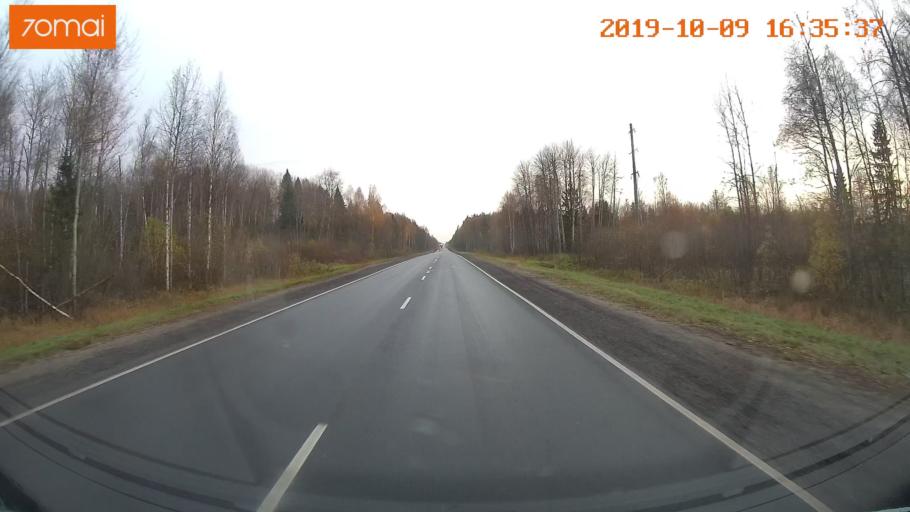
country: RU
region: Kostroma
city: Volgorechensk
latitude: 57.5530
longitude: 41.0029
